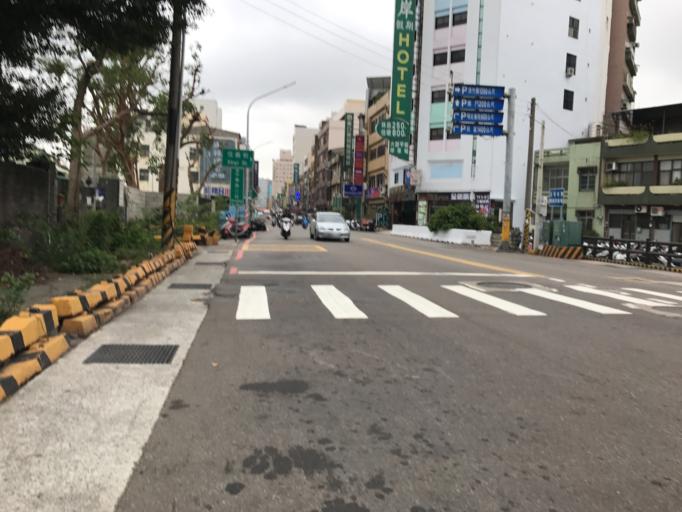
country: TW
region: Taiwan
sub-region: Hsinchu
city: Hsinchu
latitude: 24.8010
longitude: 120.9699
